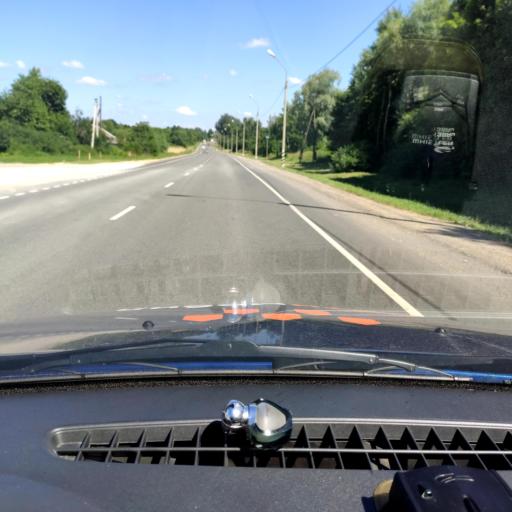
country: RU
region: Orjol
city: Kolpny
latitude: 52.4794
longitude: 37.1642
